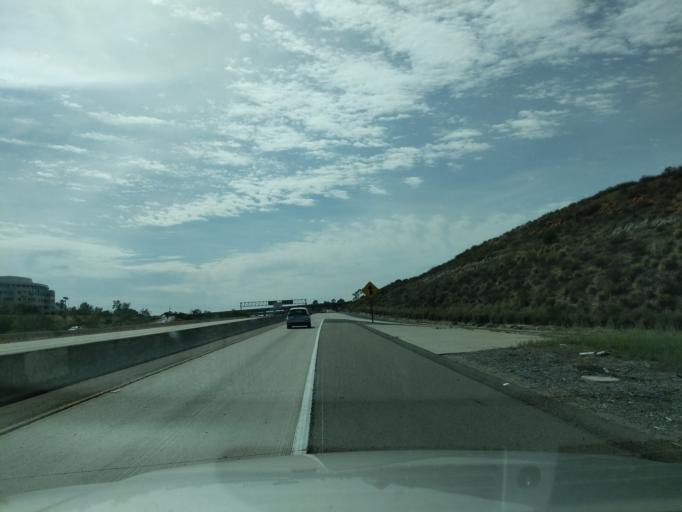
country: US
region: California
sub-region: San Diego County
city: La Mesa
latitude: 32.8421
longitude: -117.1228
